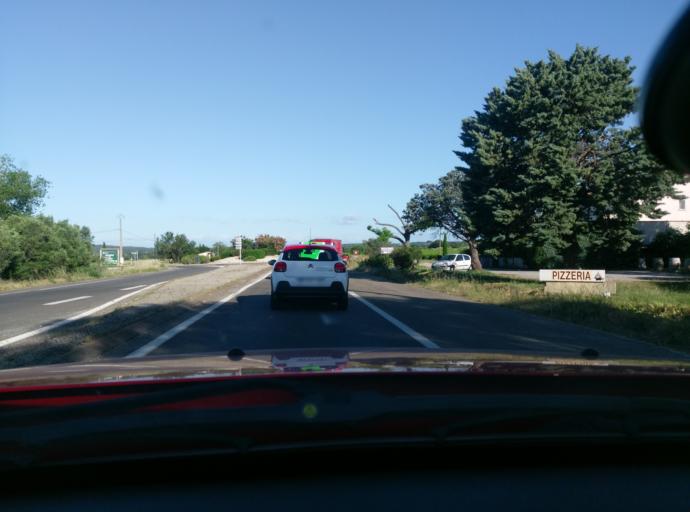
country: FR
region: Languedoc-Roussillon
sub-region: Departement du Gard
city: Uzes
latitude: 43.9867
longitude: 4.4512
